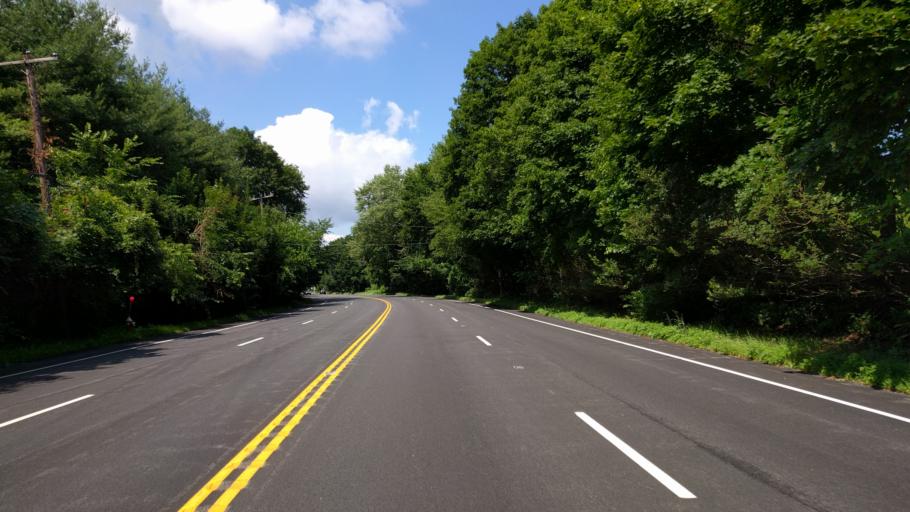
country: US
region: New York
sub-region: Nassau County
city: Brookville
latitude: 40.8267
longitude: -73.5836
